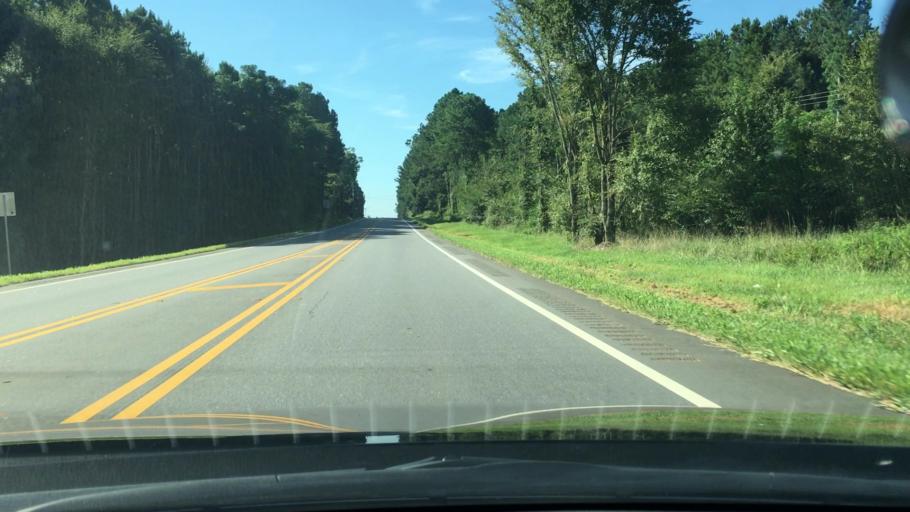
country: US
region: Georgia
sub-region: Putnam County
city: Jefferson
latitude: 33.4637
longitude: -83.4141
